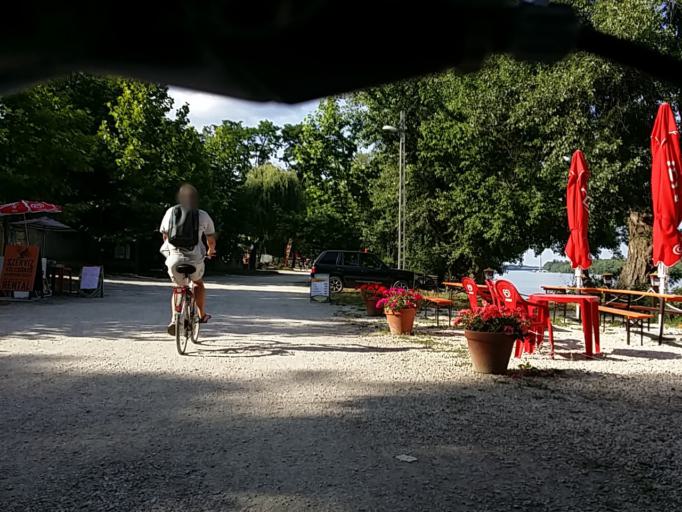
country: HU
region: Budapest
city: Budapest IV. keruelet
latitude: 47.5708
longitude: 19.0652
